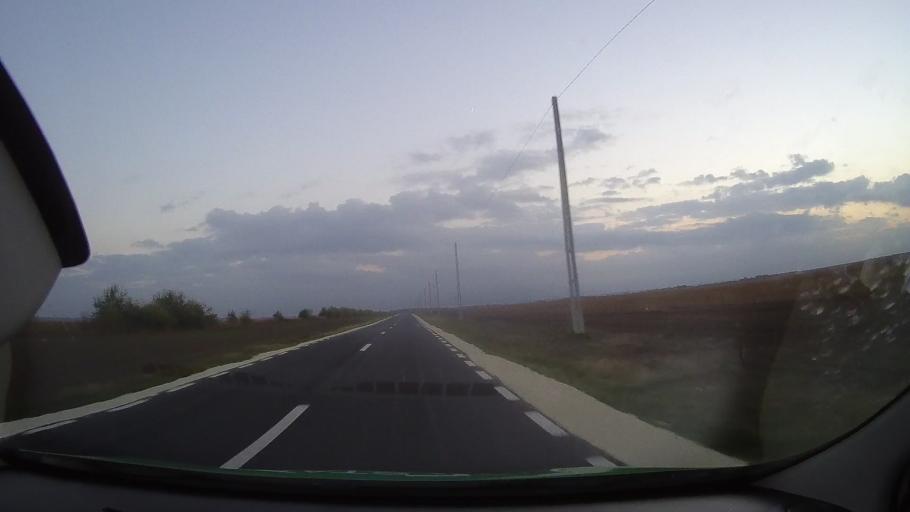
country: RO
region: Constanta
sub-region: Comuna Oltina
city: Oltina
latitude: 44.1282
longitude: 27.6684
